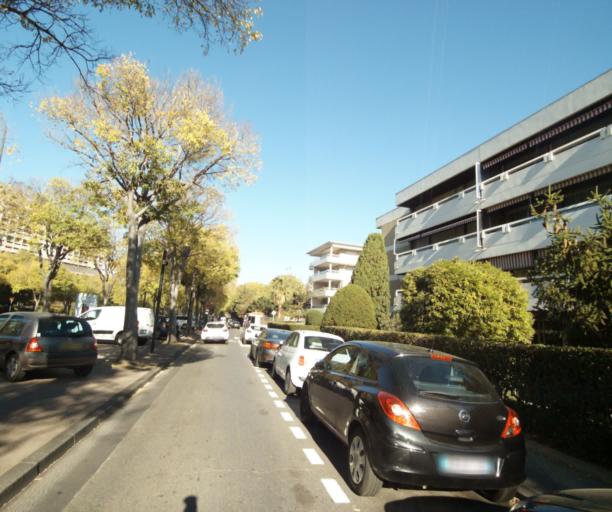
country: FR
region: Provence-Alpes-Cote d'Azur
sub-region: Departement des Bouches-du-Rhone
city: Marseille 09
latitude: 43.2600
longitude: 5.3986
